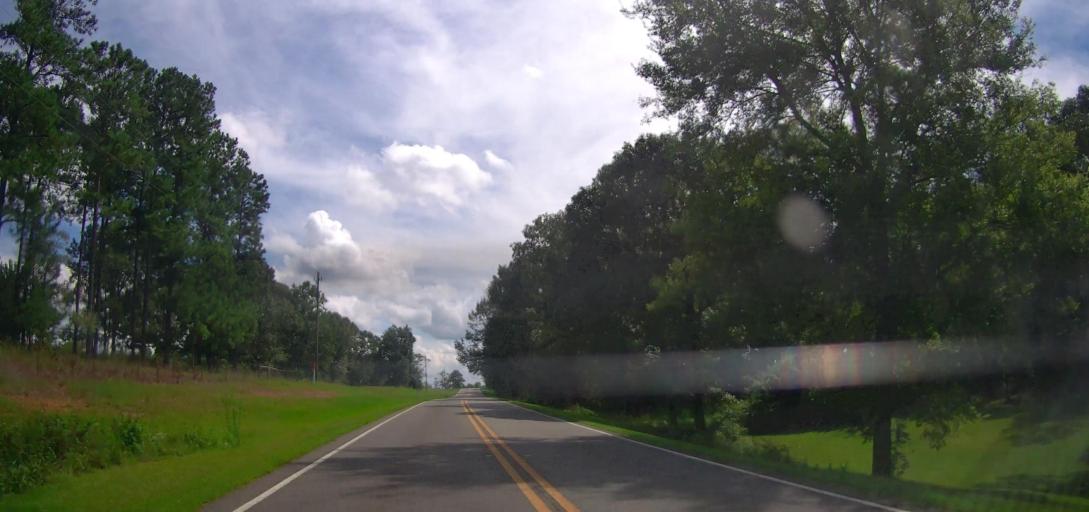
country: US
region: Georgia
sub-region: Taylor County
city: Butler
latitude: 32.5238
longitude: -84.2061
